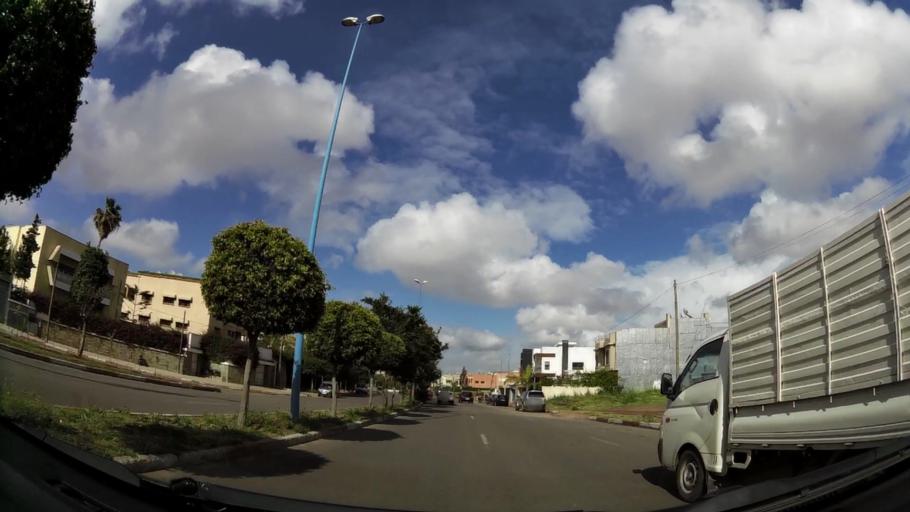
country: MA
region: Grand Casablanca
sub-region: Casablanca
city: Casablanca
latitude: 33.5462
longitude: -7.6068
